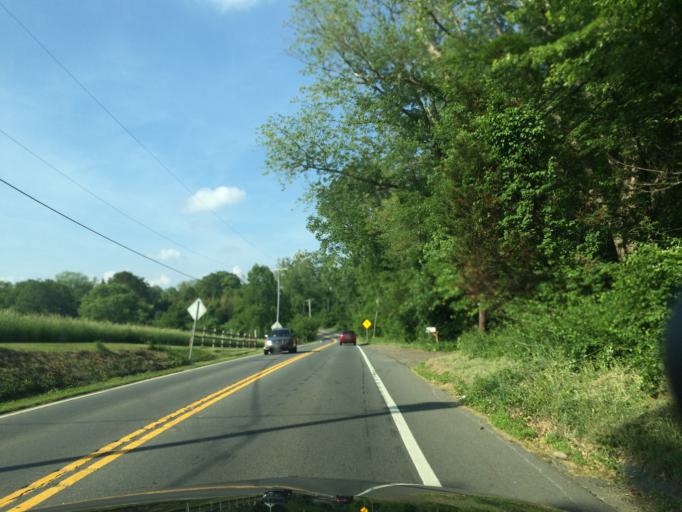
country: US
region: Maryland
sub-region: Montgomery County
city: Olney
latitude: 39.2111
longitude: -77.0625
